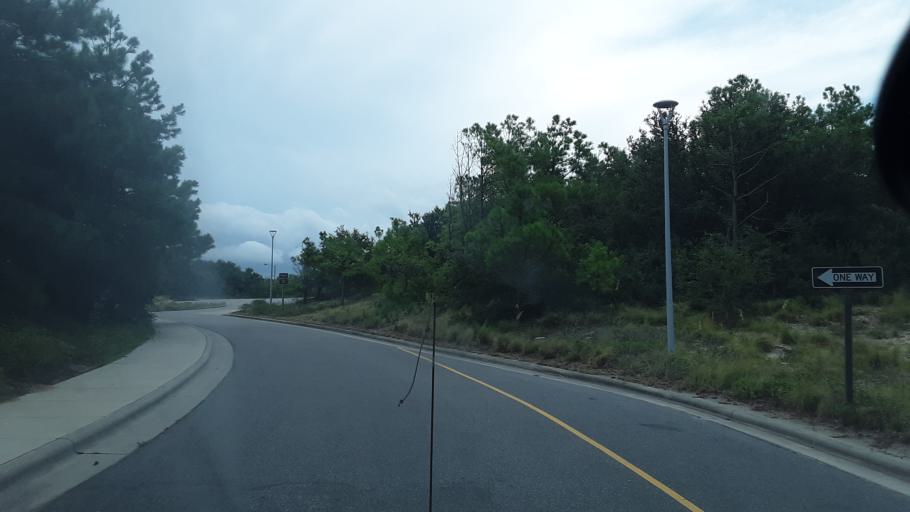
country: US
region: North Carolina
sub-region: Dare County
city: Kitty Hawk
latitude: 36.0980
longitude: -75.7156
